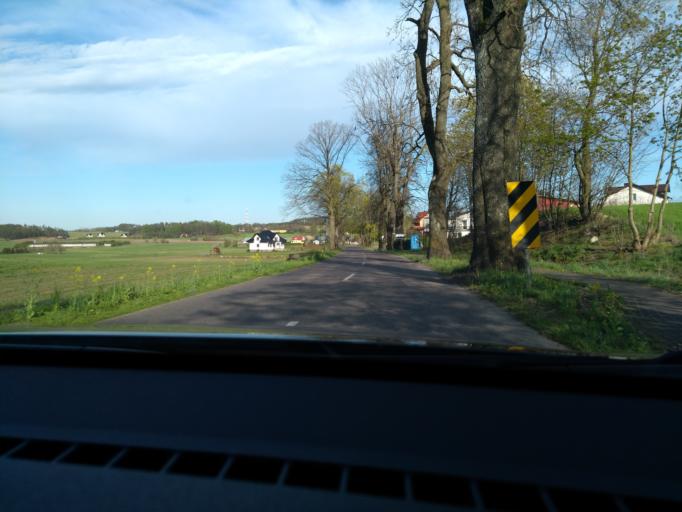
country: PL
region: Pomeranian Voivodeship
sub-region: Powiat kartuski
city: Suleczyno
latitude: 54.3276
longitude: 17.7826
